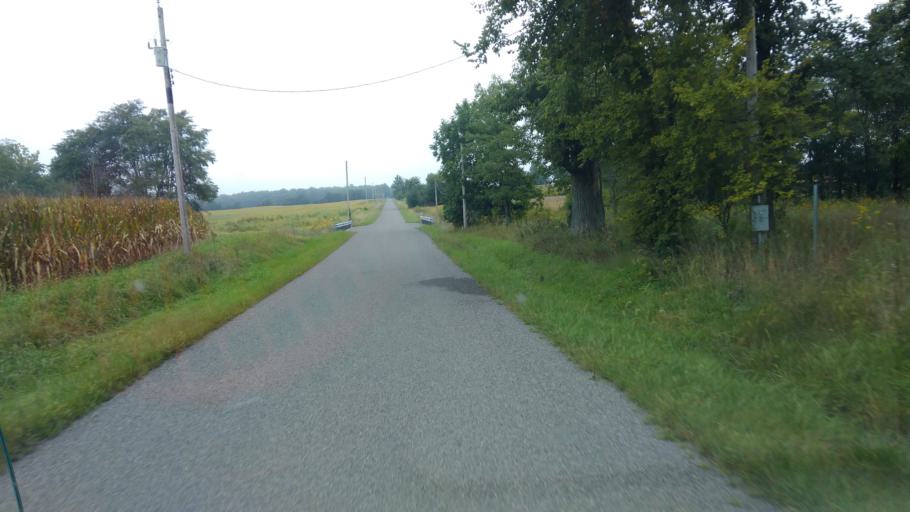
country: US
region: Ohio
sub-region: Logan County
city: Northwood
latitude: 40.4553
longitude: -83.5668
